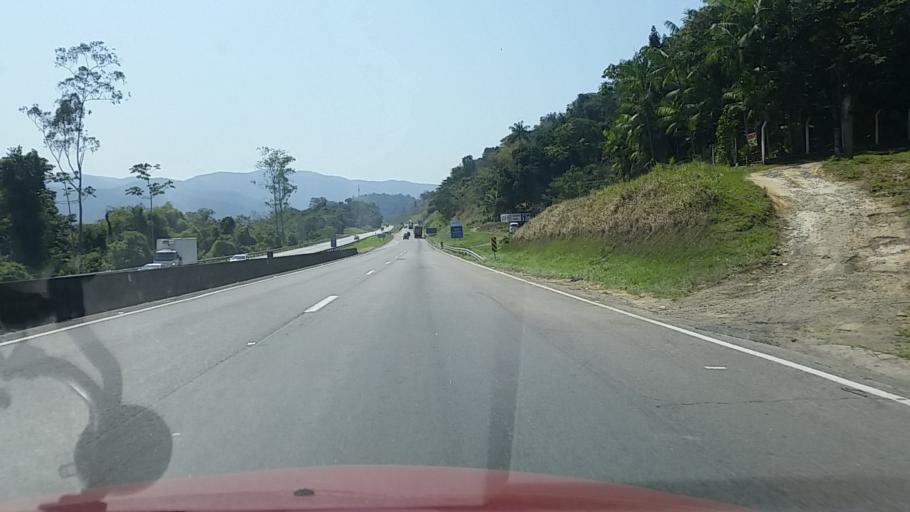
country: BR
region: Sao Paulo
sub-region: Miracatu
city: Miracatu
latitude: -24.1666
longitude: -47.3342
